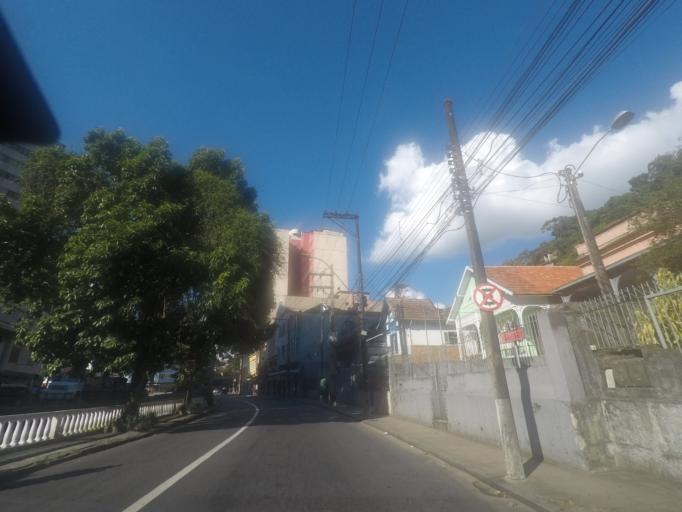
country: BR
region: Rio de Janeiro
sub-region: Petropolis
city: Petropolis
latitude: -22.5098
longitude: -43.1696
